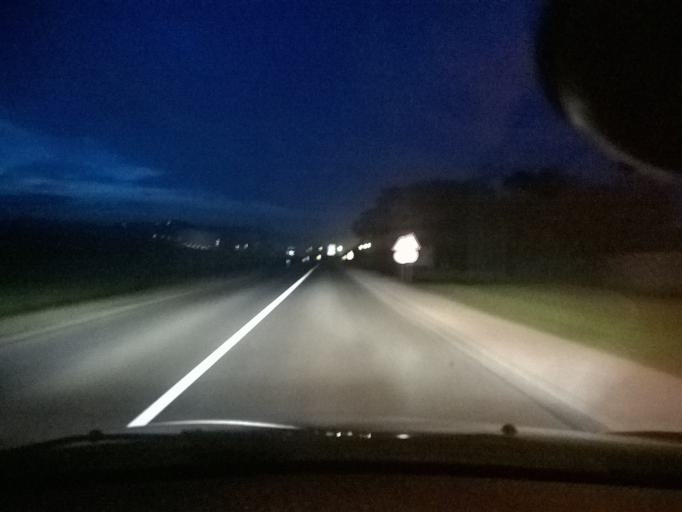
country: HR
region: Krapinsko-Zagorska
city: Zabok
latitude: 46.0791
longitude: 15.9170
